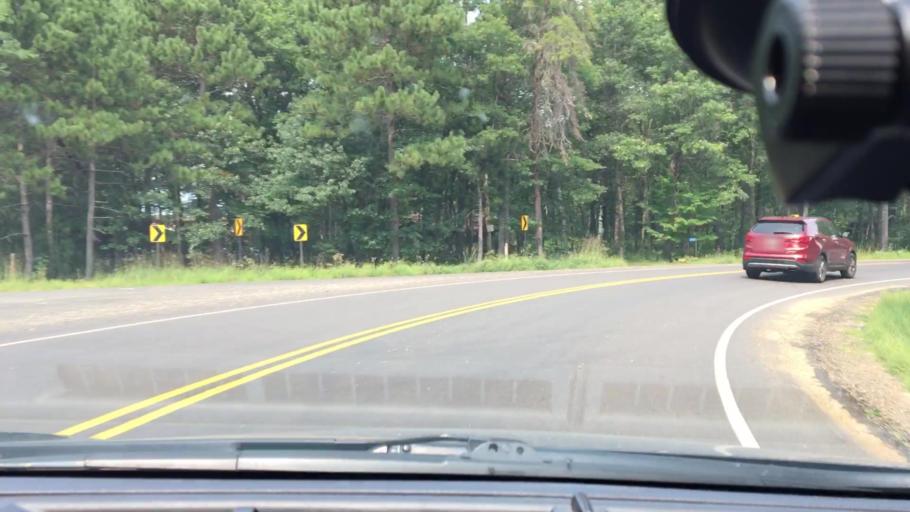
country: US
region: Minnesota
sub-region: Crow Wing County
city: Breezy Point
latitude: 46.5333
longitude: -94.1824
